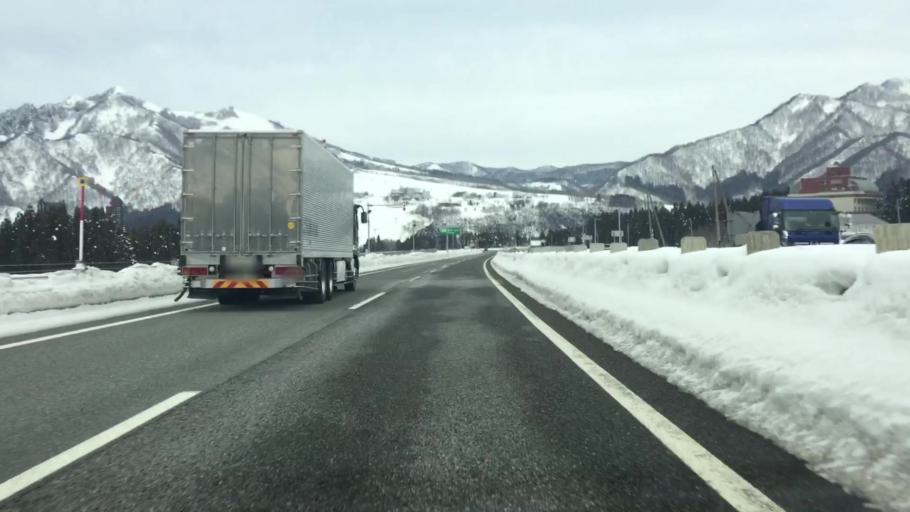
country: JP
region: Niigata
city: Shiozawa
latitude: 36.9180
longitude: 138.8400
